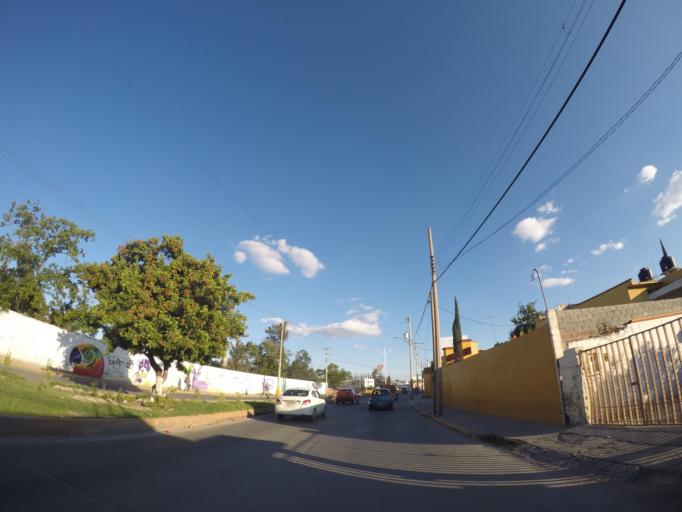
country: MX
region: San Luis Potosi
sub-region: San Luis Potosi
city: San Luis Potosi
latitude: 22.1689
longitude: -100.9812
